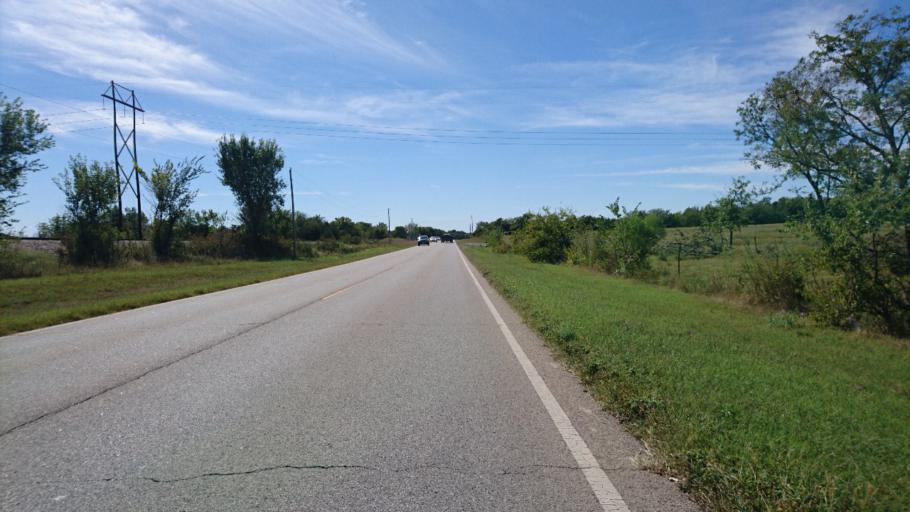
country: US
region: Oklahoma
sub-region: Lincoln County
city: Stroud
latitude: 35.7422
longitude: -96.7041
